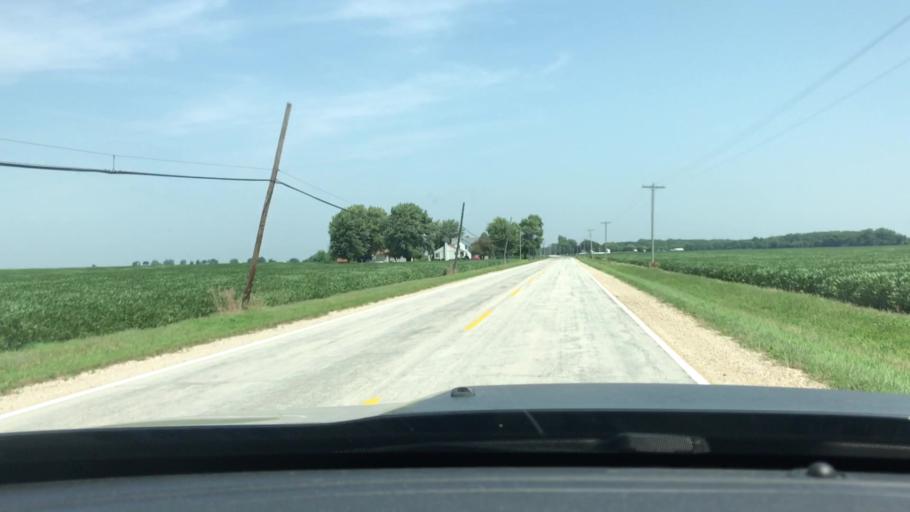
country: US
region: Illinois
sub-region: LaSalle County
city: Sheridan
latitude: 41.5090
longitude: -88.7273
